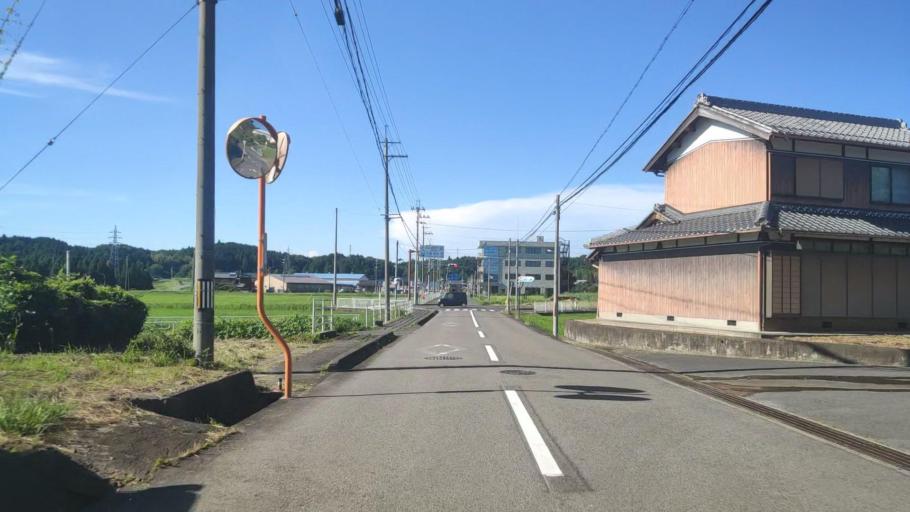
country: JP
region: Shiga Prefecture
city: Minakuchicho-matoba
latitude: 34.9048
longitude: 136.2161
